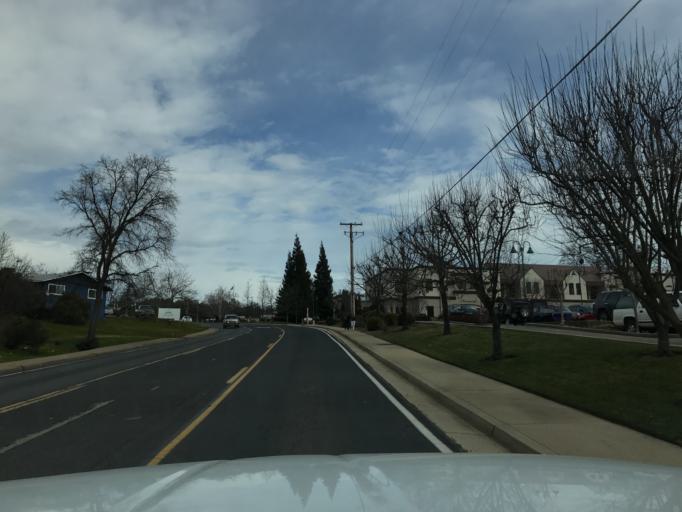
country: US
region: California
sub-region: Calaveras County
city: San Andreas
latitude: 38.1895
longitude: -120.6720
